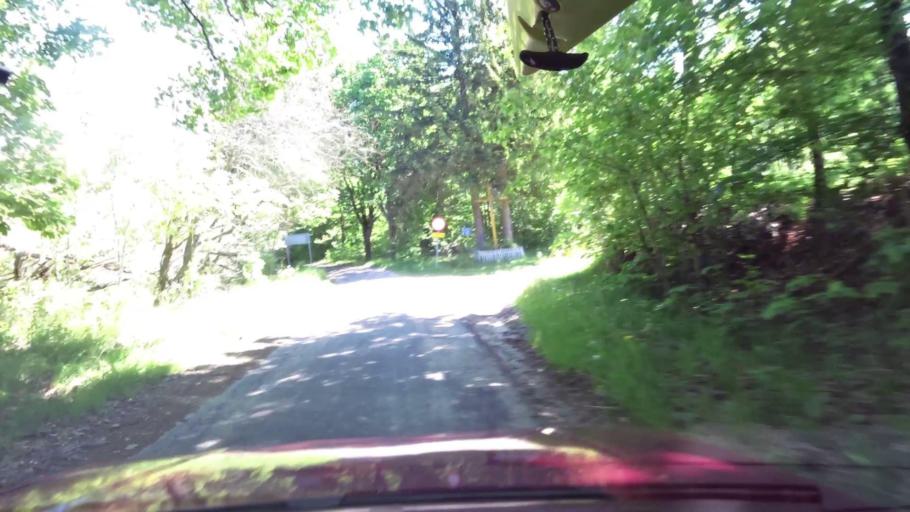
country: PL
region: West Pomeranian Voivodeship
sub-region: Powiat koszalinski
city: Polanow
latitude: 54.0366
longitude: 16.7781
